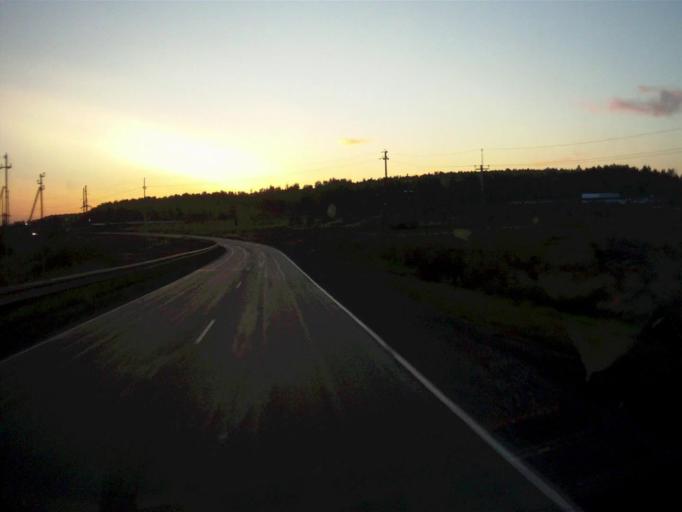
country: RU
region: Chelyabinsk
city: Poletayevo
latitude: 55.2249
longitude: 60.9994
